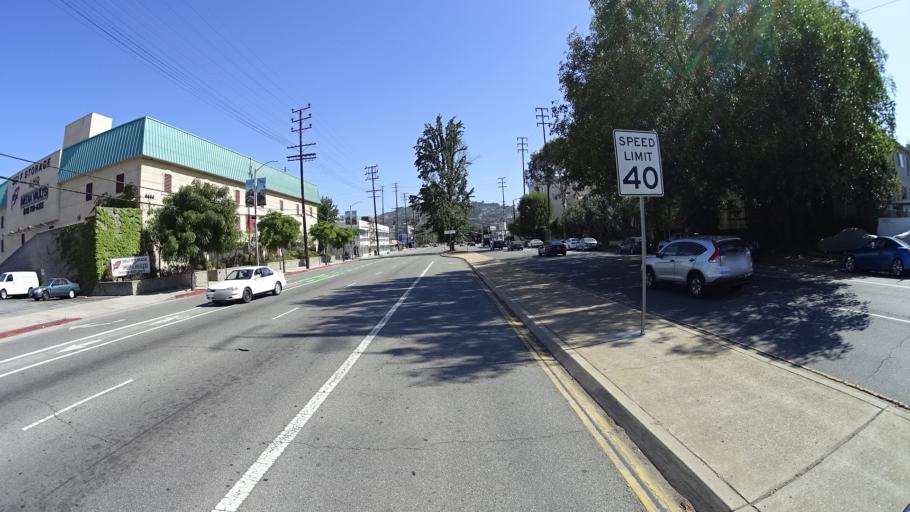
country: US
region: California
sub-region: Los Angeles County
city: Universal City
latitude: 34.1521
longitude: -118.3703
